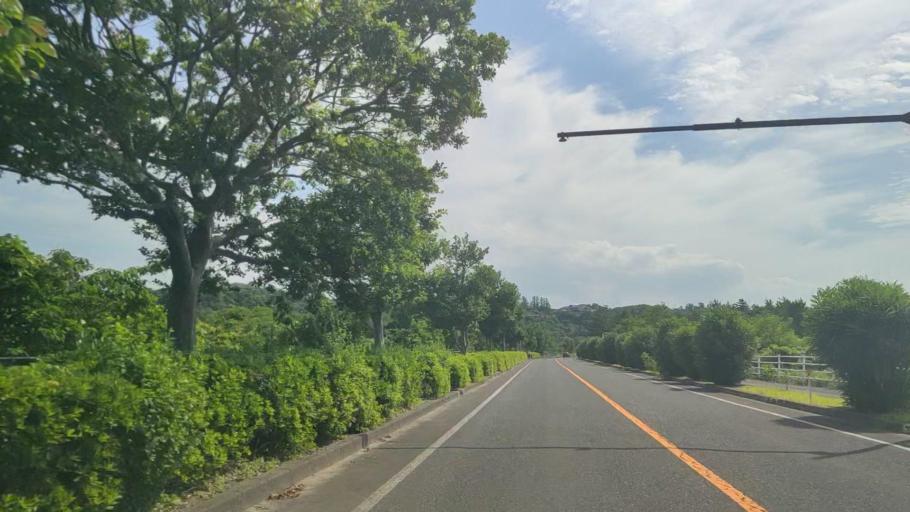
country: JP
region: Tottori
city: Tottori
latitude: 35.5374
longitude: 134.2352
